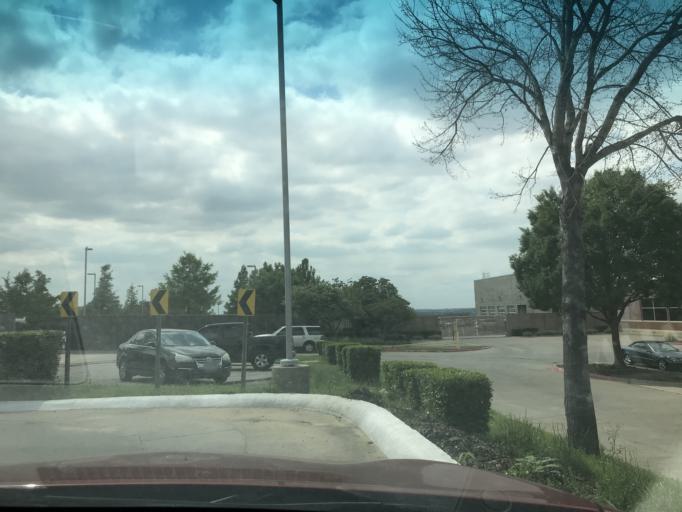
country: US
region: Texas
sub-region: Tarrant County
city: Benbrook
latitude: 32.6655
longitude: -97.4215
